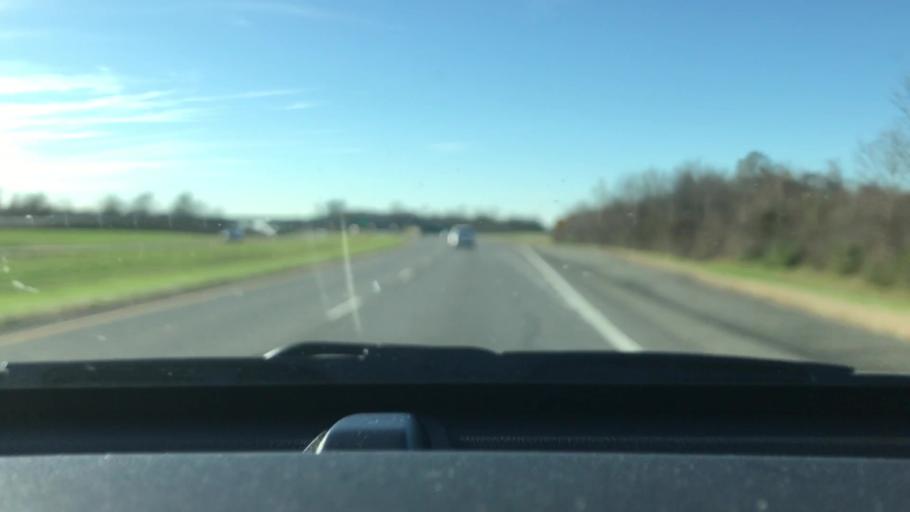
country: US
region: Louisiana
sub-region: Rapides Parish
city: Boyce
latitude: 31.3795
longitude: -92.6488
